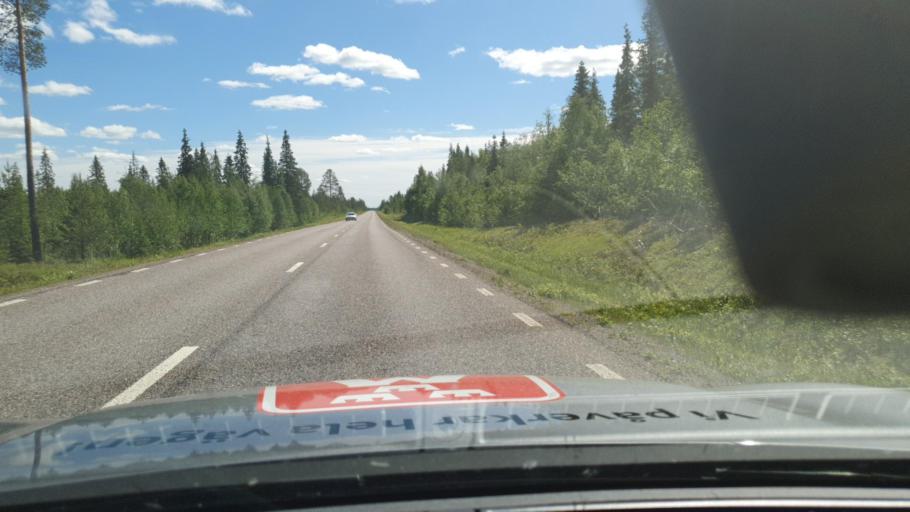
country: SE
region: Norrbotten
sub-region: Pajala Kommun
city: Pajala
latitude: 67.1569
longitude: 23.5505
